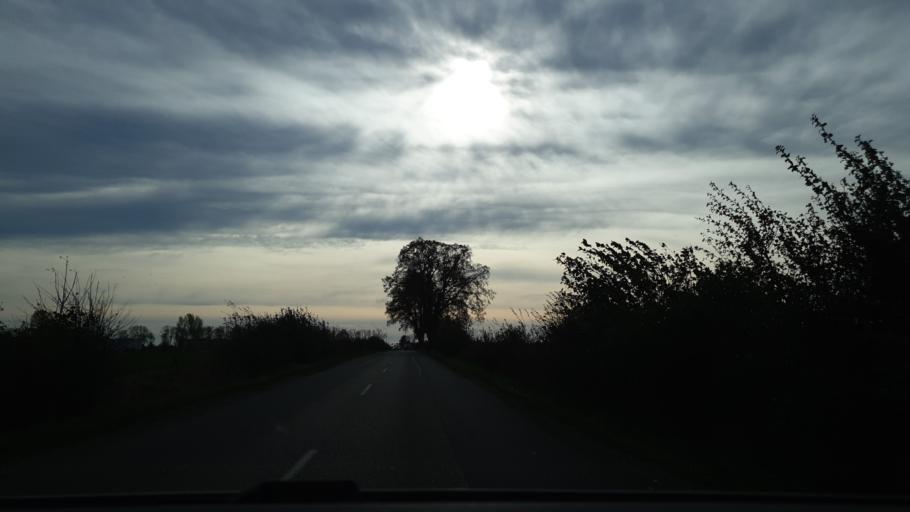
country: PL
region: Pomeranian Voivodeship
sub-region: Powiat pucki
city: Puck
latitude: 54.6906
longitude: 18.3666
